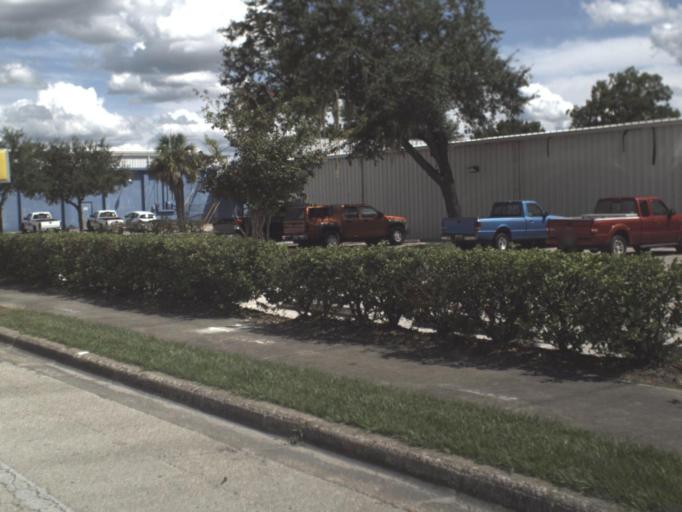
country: US
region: Florida
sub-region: Polk County
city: Mulberry
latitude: 27.8949
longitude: -81.9767
